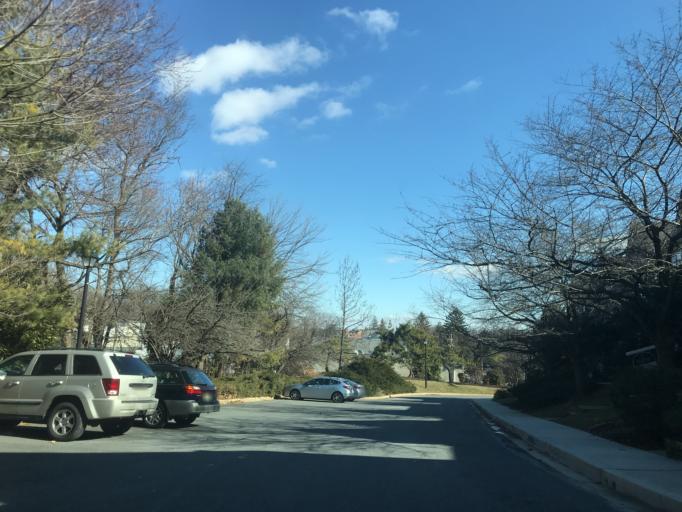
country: US
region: Maryland
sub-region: City of Baltimore
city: Baltimore
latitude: 39.3441
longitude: -76.6326
